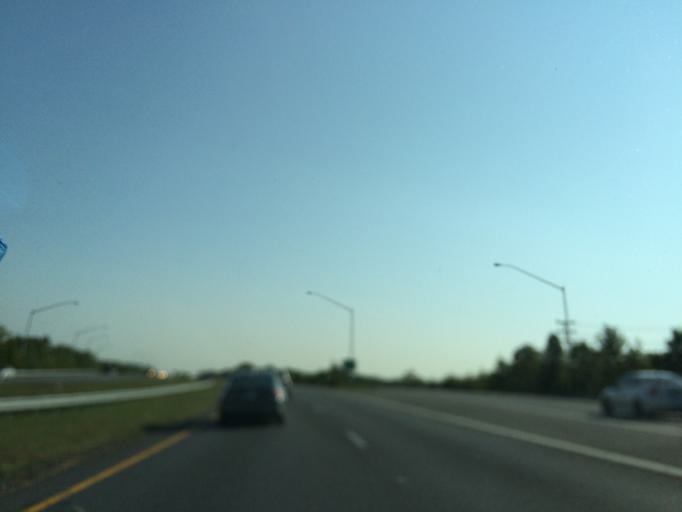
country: US
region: Maryland
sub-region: Anne Arundel County
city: Odenton
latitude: 39.0885
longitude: -76.7213
